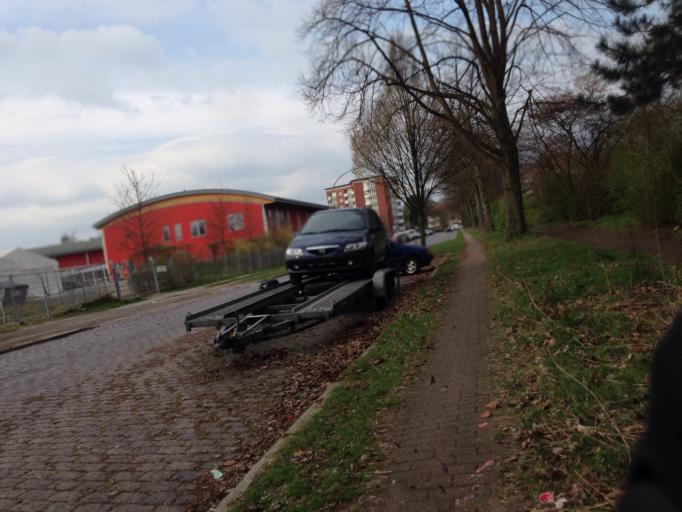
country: DE
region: Hamburg
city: Marienthal
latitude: 53.5871
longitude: 10.0746
